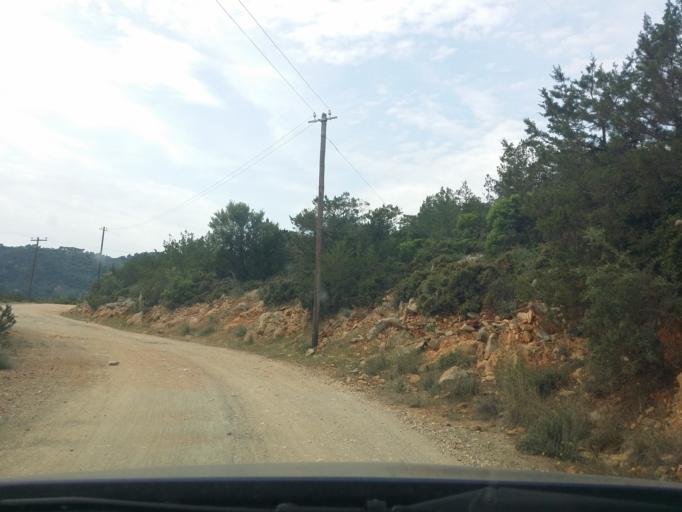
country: GR
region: Attica
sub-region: Nomos Piraios
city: Poros
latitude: 37.5385
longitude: 23.4819
